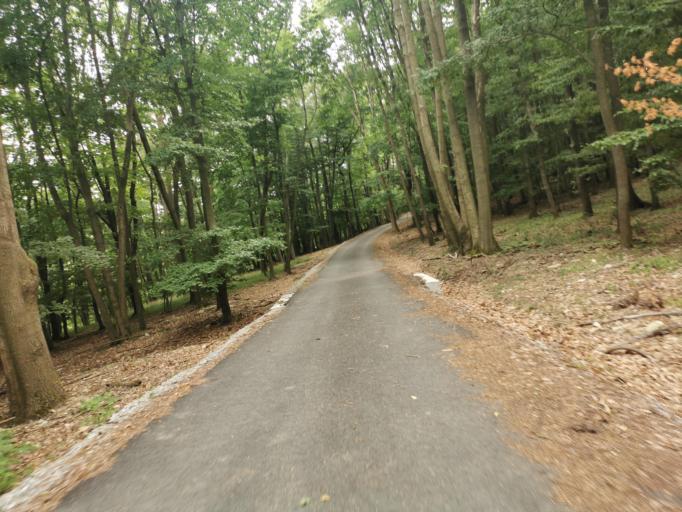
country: SK
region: Trenciansky
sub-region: Okres Myjava
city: Myjava
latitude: 48.7284
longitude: 17.5134
